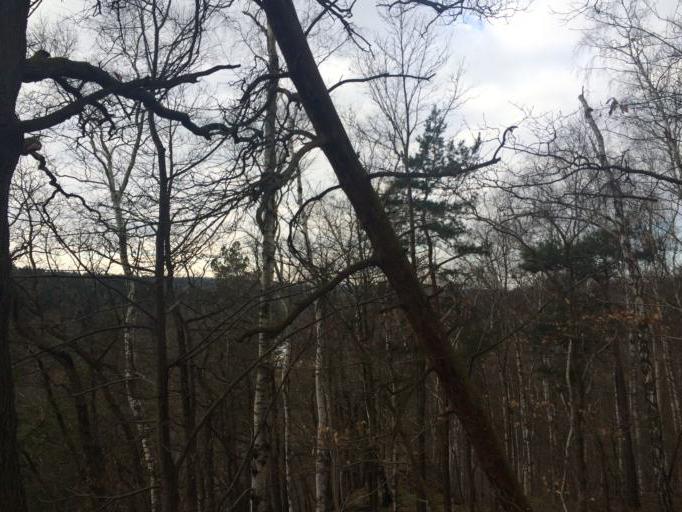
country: PL
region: Lower Silesian Voivodeship
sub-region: Powiat lwowecki
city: Lwowek Slaski
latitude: 51.1051
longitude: 15.6241
